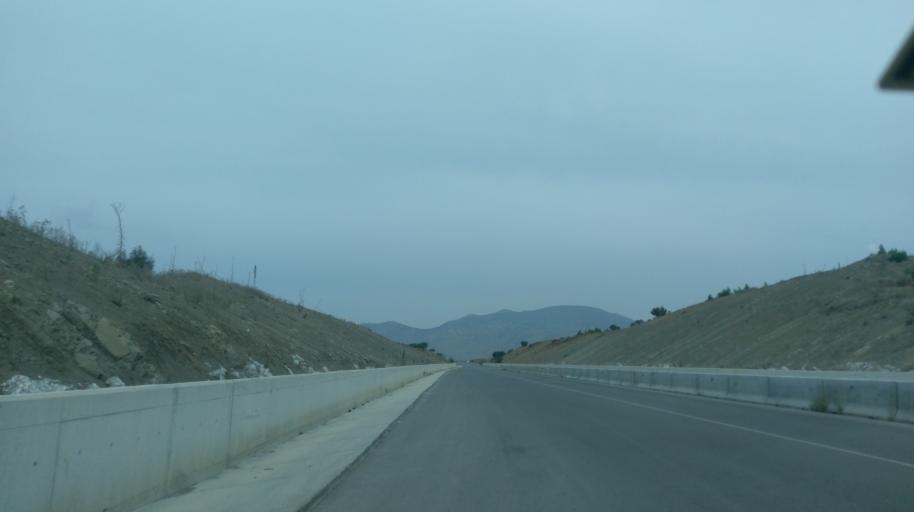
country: CY
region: Lefkosia
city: Nicosia
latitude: 35.2390
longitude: 33.3258
